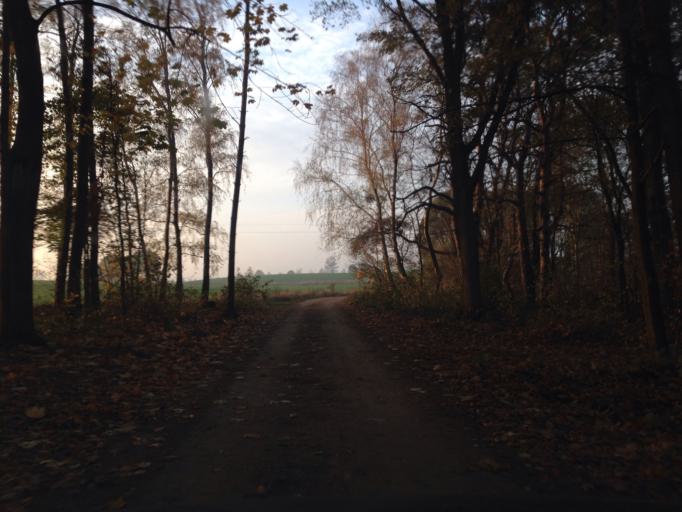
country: PL
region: Warmian-Masurian Voivodeship
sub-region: Powiat dzialdowski
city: Lidzbark
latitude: 53.2601
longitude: 19.7741
